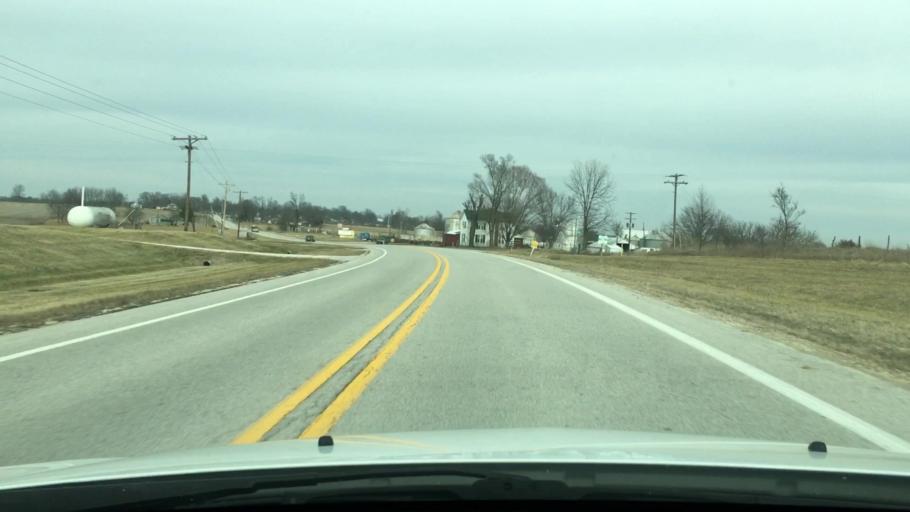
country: US
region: Illinois
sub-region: Pike County
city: Pittsfield
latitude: 39.5333
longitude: -90.9209
